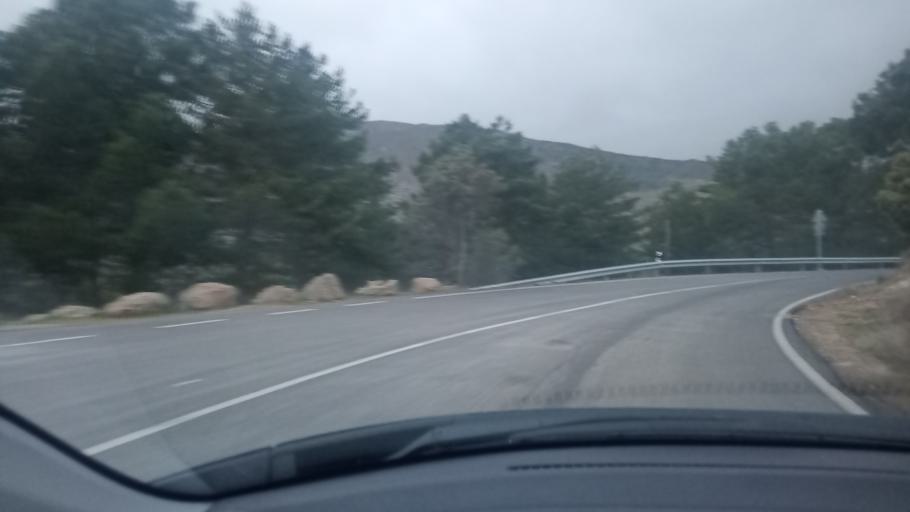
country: ES
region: Madrid
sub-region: Provincia de Madrid
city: Zarzalejo
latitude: 40.5512
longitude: -4.1949
